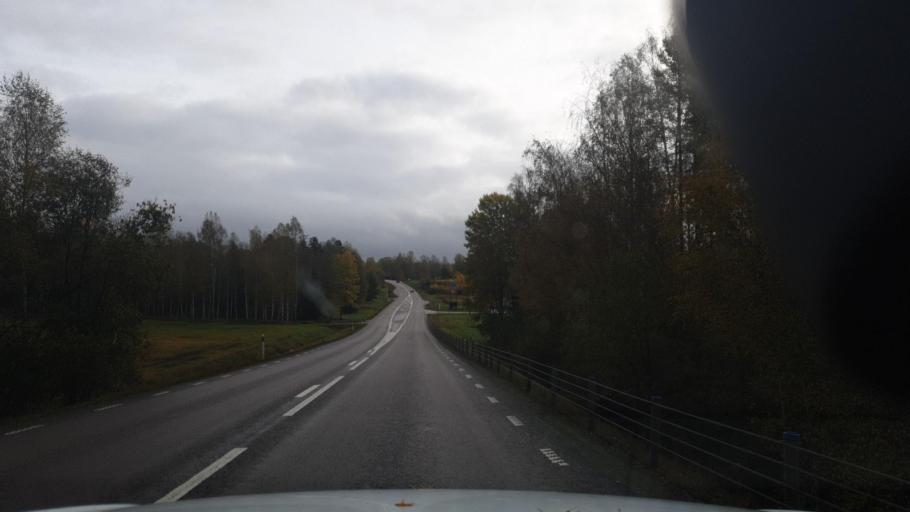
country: SE
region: Vaermland
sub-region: Arvika Kommun
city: Arvika
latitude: 59.6647
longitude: 12.8792
